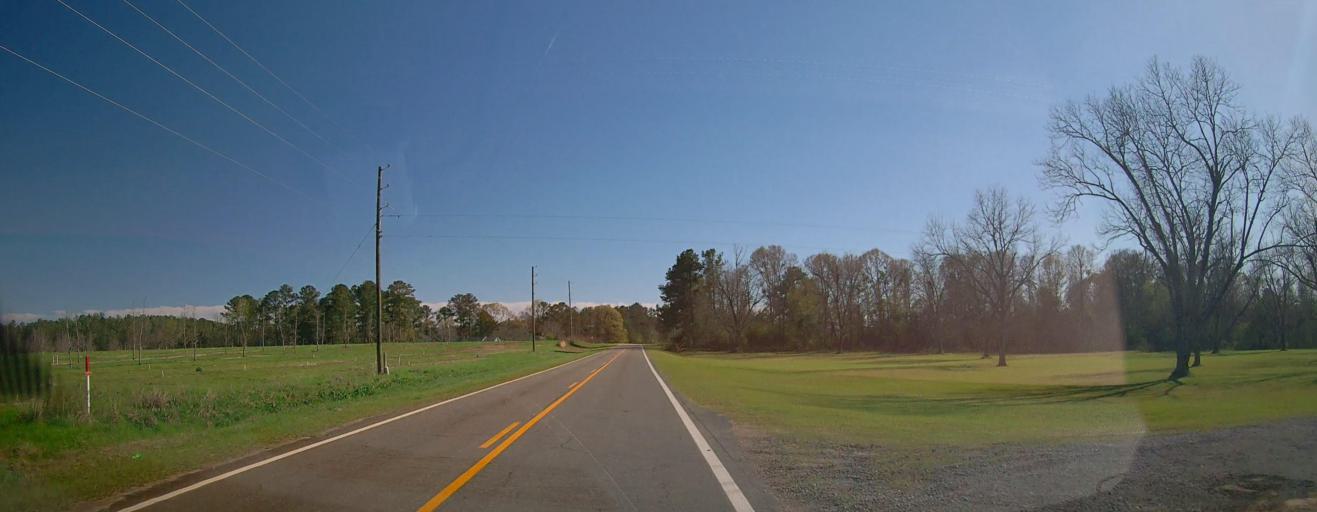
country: US
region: Georgia
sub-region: Peach County
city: Fort Valley
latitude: 32.6057
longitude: -83.9828
